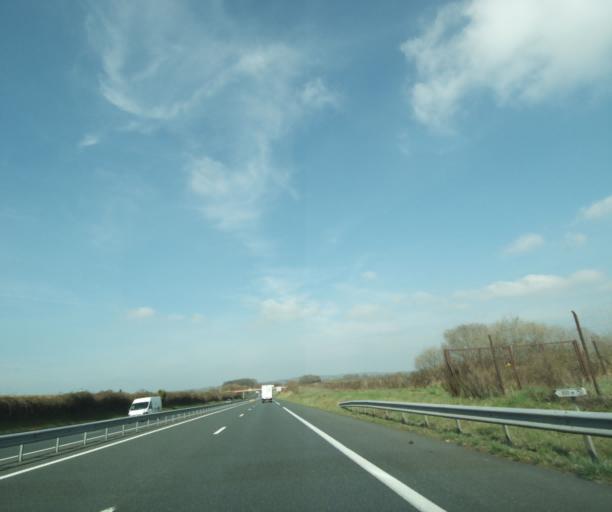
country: FR
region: Centre
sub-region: Departement de l'Indre
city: Le Pechereau
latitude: 46.4941
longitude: 1.4986
